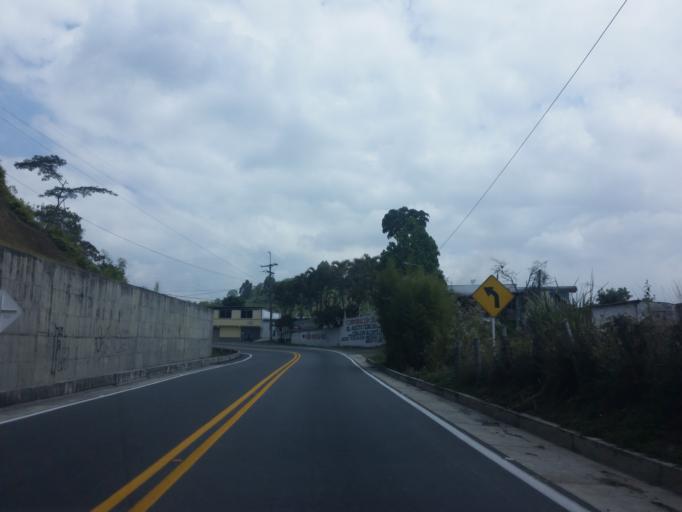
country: CO
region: Caldas
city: Villamaria
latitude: 5.0128
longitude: -75.5454
